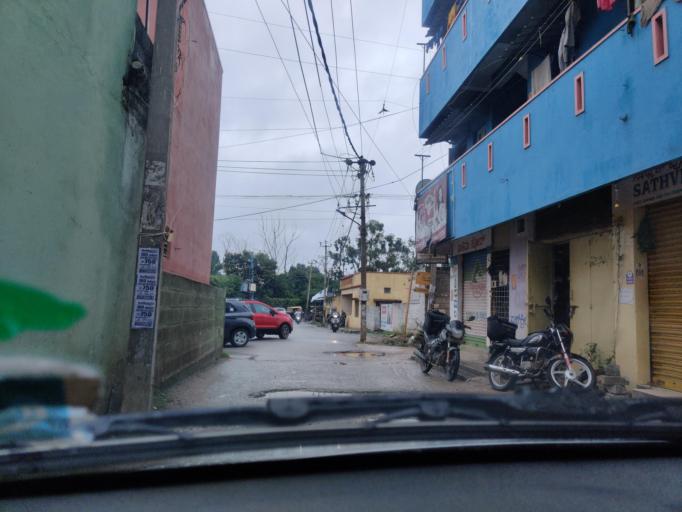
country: IN
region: Karnataka
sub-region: Bangalore Urban
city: Bangalore
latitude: 13.0280
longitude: 77.6427
